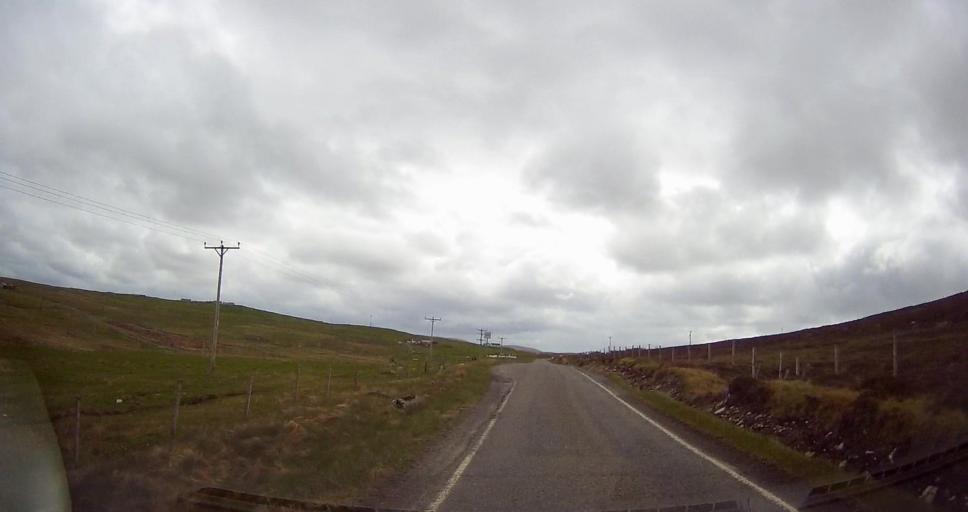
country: GB
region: Scotland
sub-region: Shetland Islands
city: Sandwick
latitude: 60.2463
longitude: -1.5106
